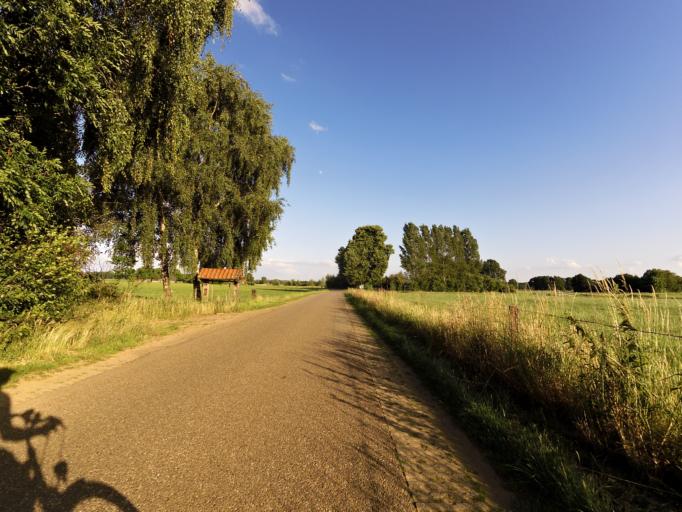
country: NL
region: Gelderland
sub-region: Oude IJsselstreek
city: Gendringen
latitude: 51.8842
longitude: 6.3997
